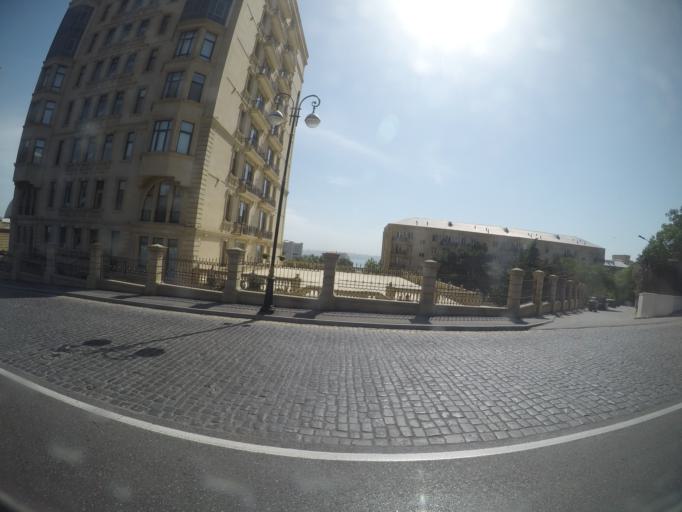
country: AZ
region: Baki
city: Badamdar
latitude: 40.3627
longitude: 49.8267
